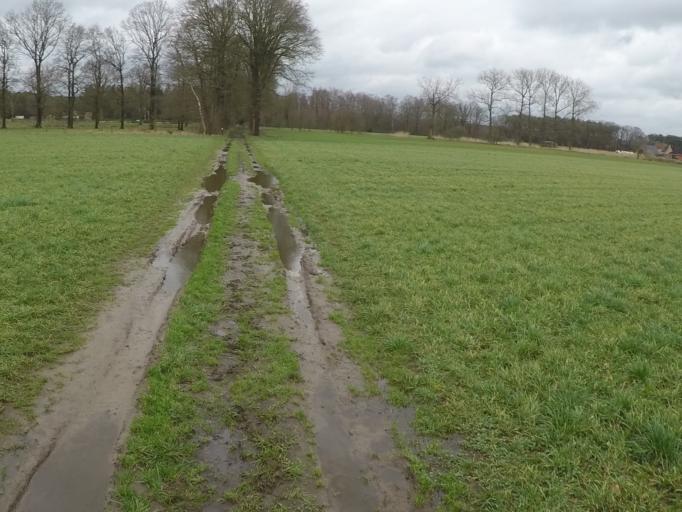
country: BE
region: Flanders
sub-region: Provincie Antwerpen
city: Zandhoven
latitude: 51.2226
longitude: 4.6241
